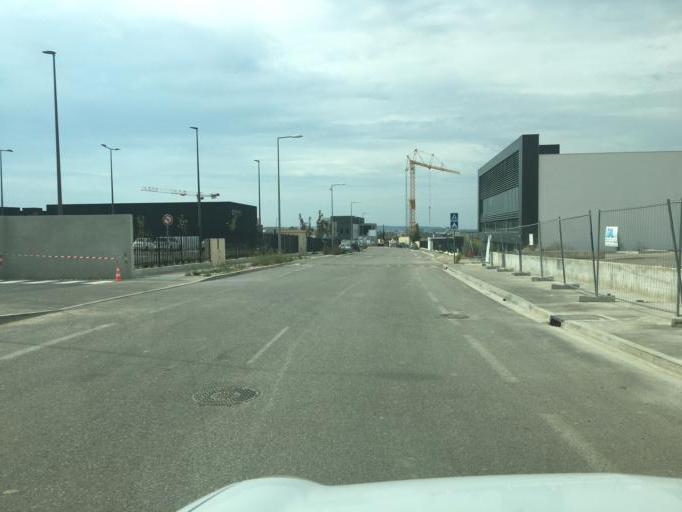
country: FR
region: Provence-Alpes-Cote d'Azur
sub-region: Departement des Bouches-du-Rhone
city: Bouc-Bel-Air
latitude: 43.4812
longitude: 5.3912
